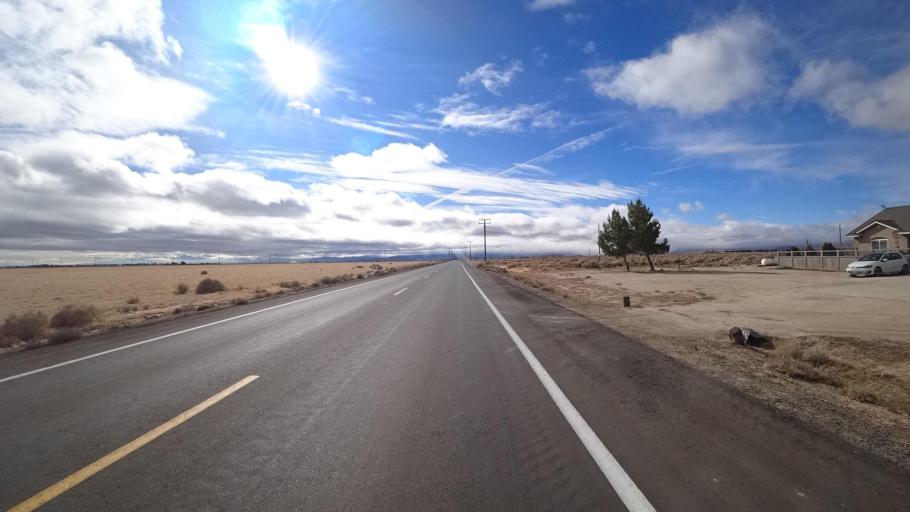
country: US
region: California
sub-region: Kern County
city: Rosamond
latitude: 34.8391
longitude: -118.2907
